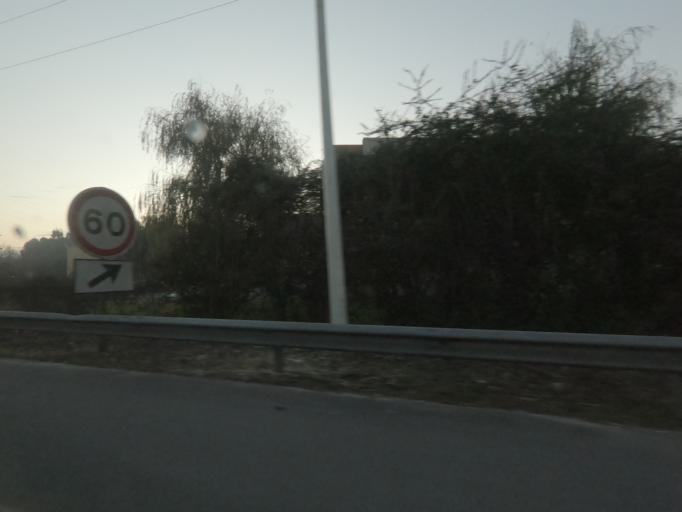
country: PT
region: Porto
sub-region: Porto
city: Porto
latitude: 41.1759
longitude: -8.6225
